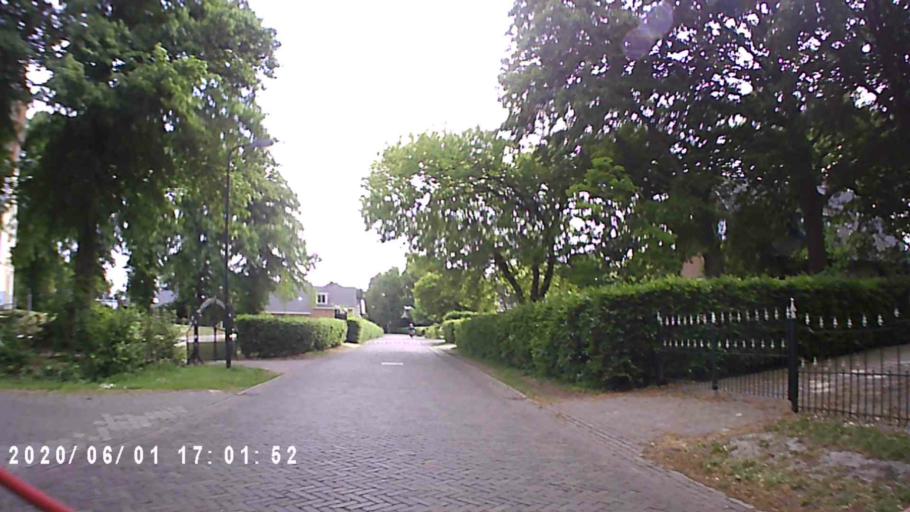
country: NL
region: Friesland
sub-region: Gemeente Tytsjerksteradiel
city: Hurdegaryp
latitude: 53.1794
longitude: 5.9272
